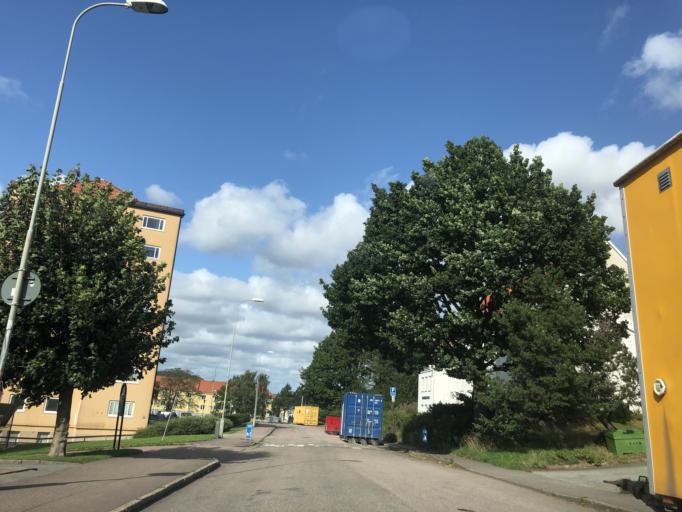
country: SE
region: Vaestra Goetaland
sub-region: Goteborg
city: Goeteborg
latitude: 57.7193
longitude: 11.9383
